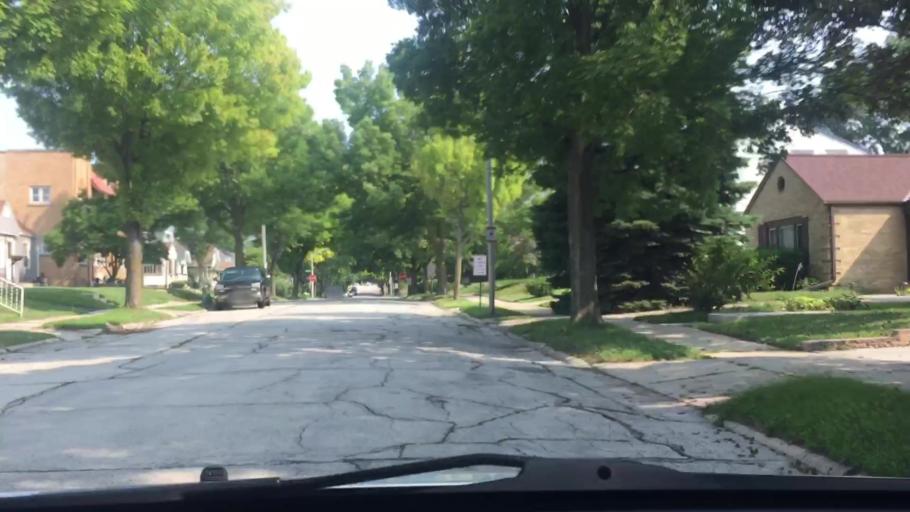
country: US
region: Wisconsin
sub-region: Milwaukee County
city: West Allis
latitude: 43.0131
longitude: -88.0244
